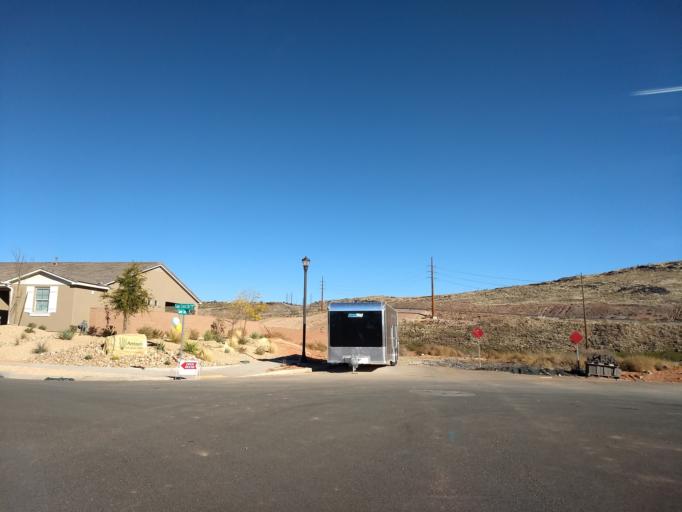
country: US
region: Utah
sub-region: Washington County
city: Washington
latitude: 37.1347
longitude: -113.4813
